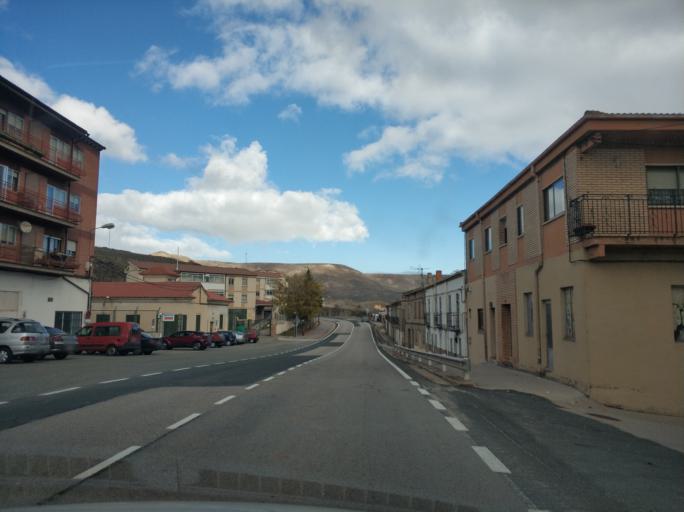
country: ES
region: Castille and Leon
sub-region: Provincia de Soria
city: Medinaceli
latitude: 41.1661
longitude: -2.4218
